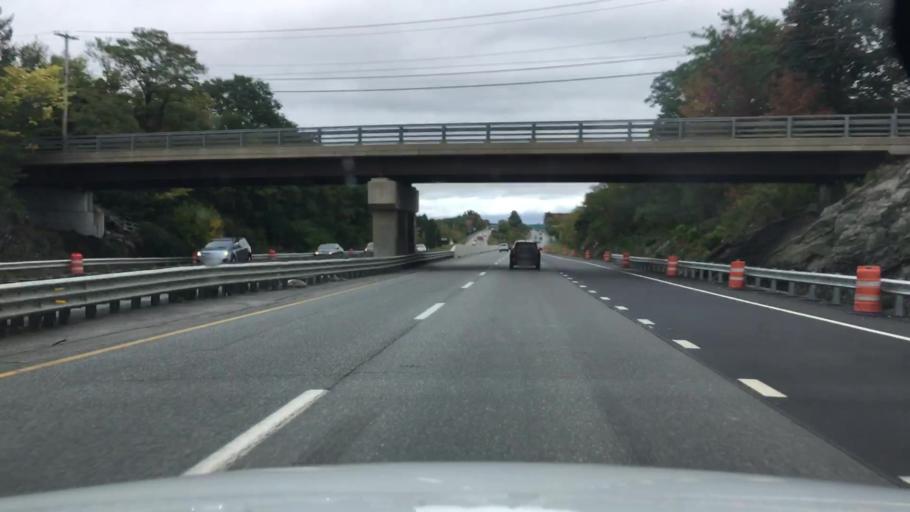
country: US
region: Maine
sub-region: Penobscot County
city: Bangor
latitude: 44.8202
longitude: -68.7696
